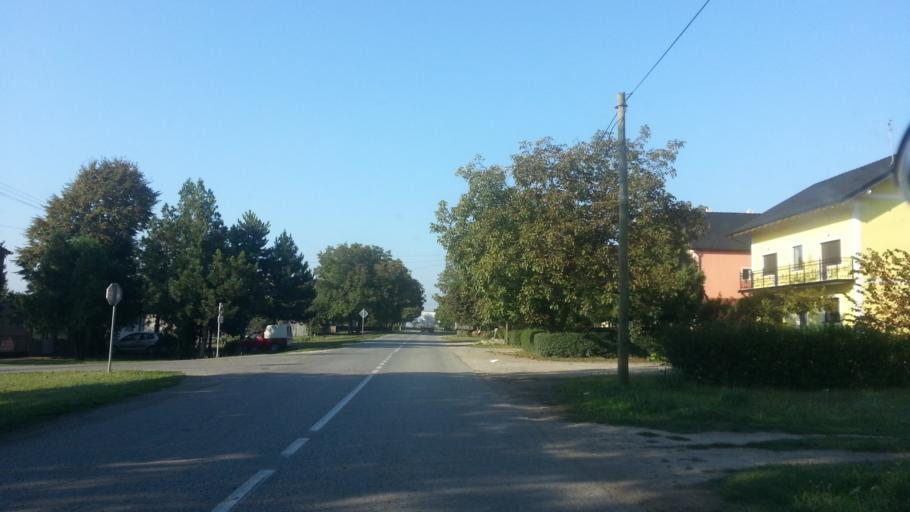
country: RS
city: Stari Banovci
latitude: 44.9786
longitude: 20.2731
